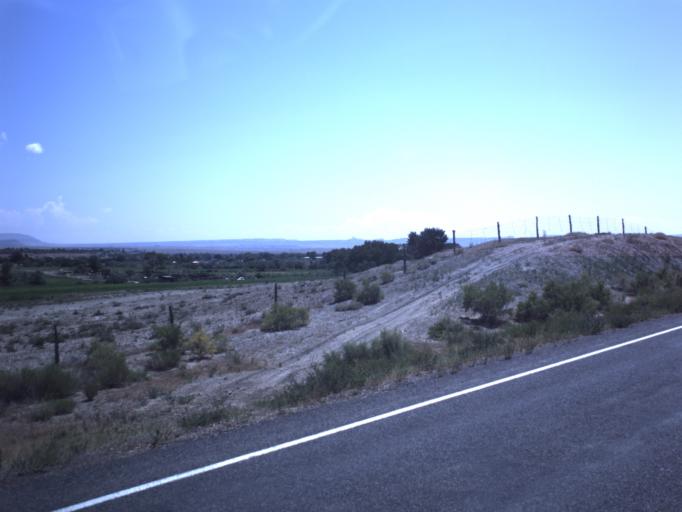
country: US
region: Utah
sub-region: Emery County
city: Orangeville
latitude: 39.2270
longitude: -111.0726
